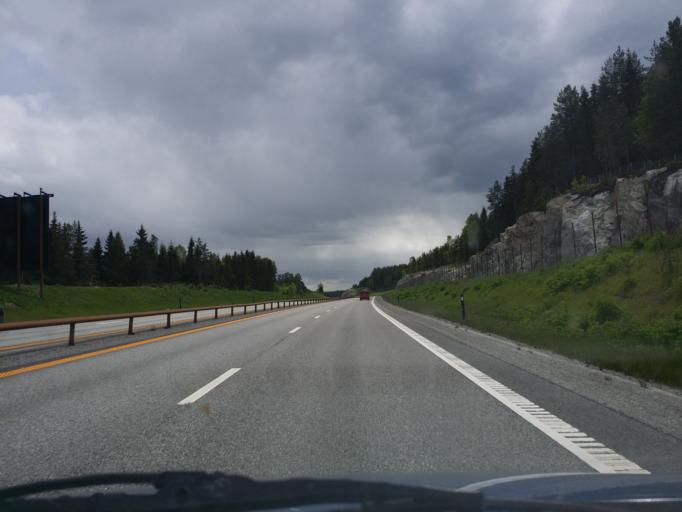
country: NO
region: Akershus
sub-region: Eidsvoll
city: Raholt
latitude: 60.3037
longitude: 11.1402
